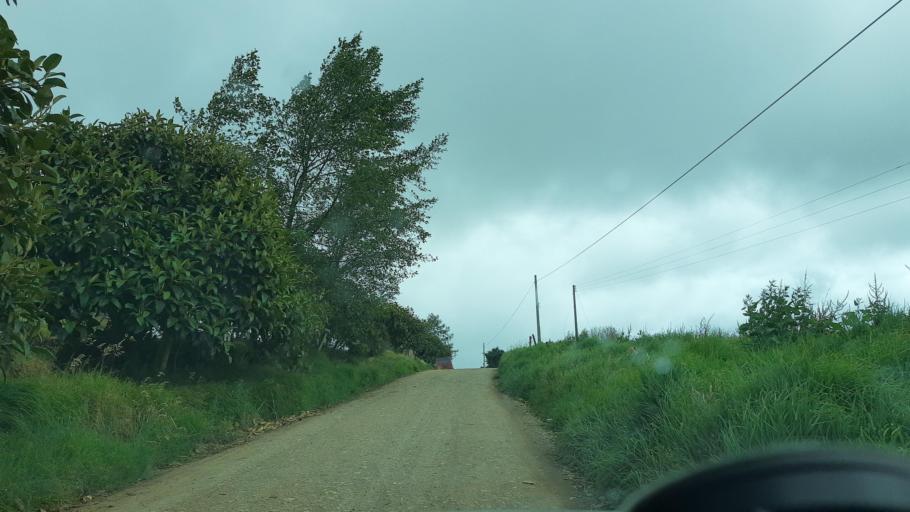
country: CO
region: Boyaca
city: Samaca
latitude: 5.4903
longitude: -73.4589
